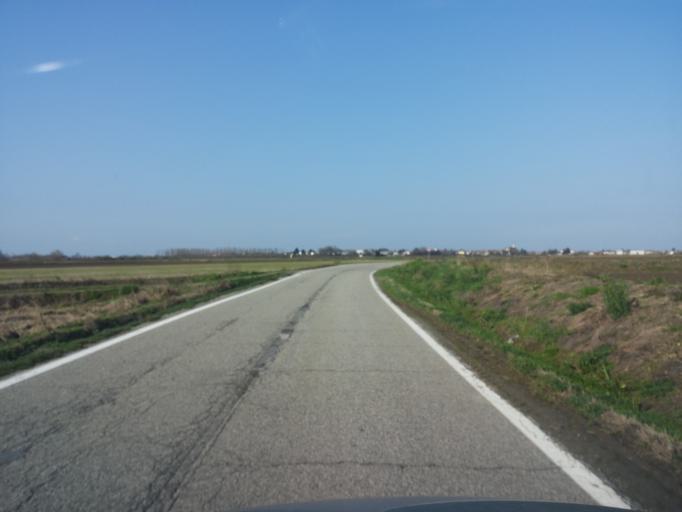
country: IT
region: Piedmont
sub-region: Provincia di Vercelli
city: Pezzana
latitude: 45.2466
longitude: 8.4897
